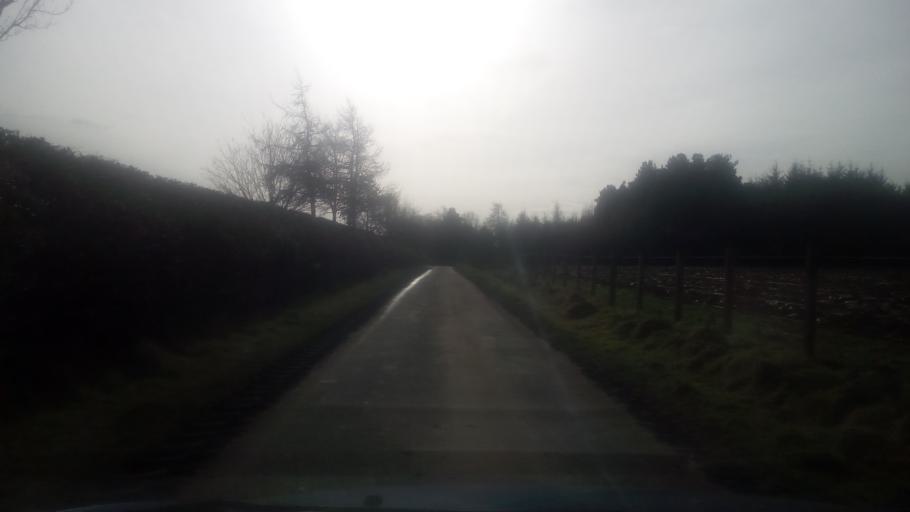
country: GB
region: Scotland
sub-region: The Scottish Borders
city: Jedburgh
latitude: 55.4373
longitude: -2.6405
